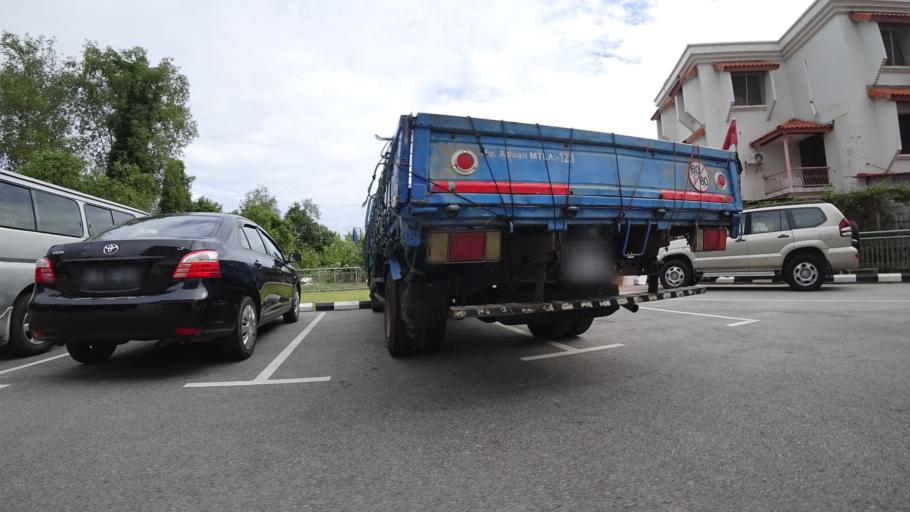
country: BN
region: Brunei and Muara
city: Bandar Seri Begawan
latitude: 4.9067
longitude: 114.9277
